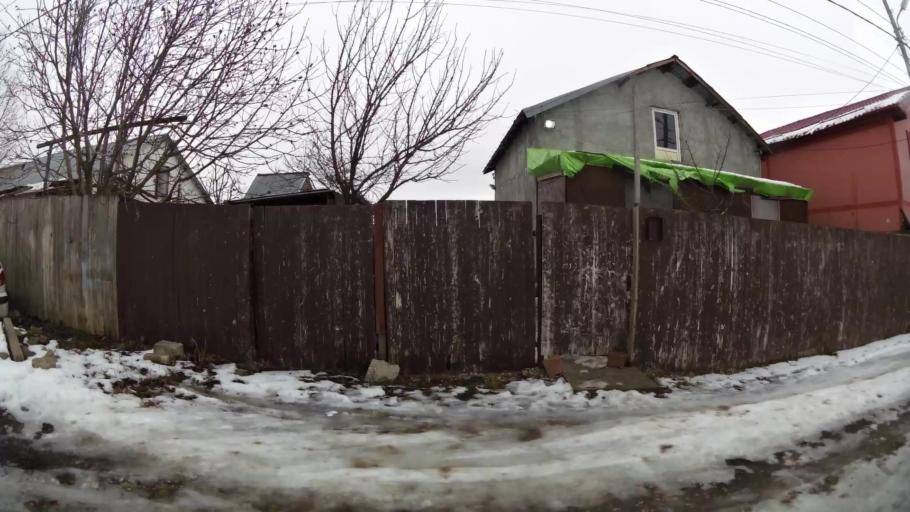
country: RO
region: Ilfov
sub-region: Comuna Pantelimon
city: Pantelimon
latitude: 44.4654
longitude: 26.2042
